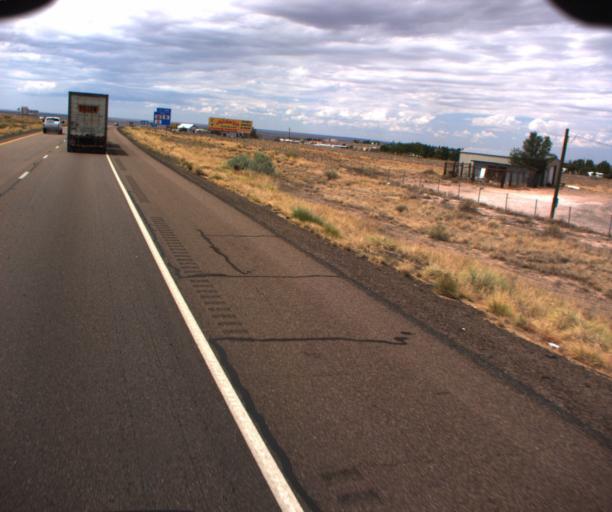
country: US
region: Arizona
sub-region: Navajo County
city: Holbrook
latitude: 34.9231
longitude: -110.1383
